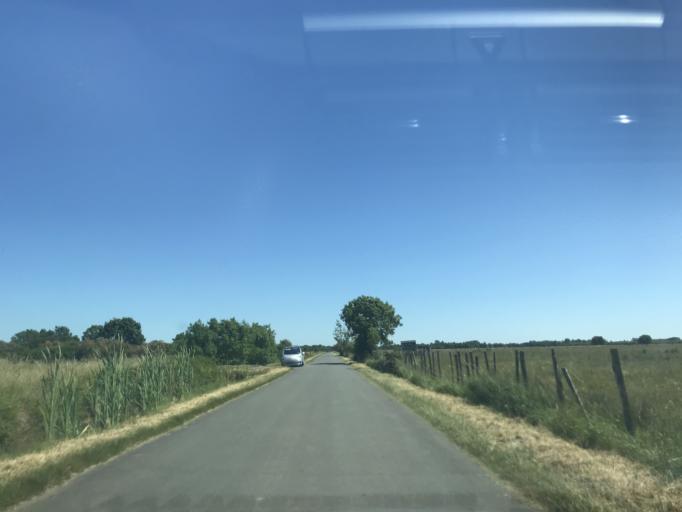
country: FR
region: Poitou-Charentes
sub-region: Departement de la Charente-Maritime
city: Mortagne-sur-Gironde
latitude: 45.4475
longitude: -0.7606
